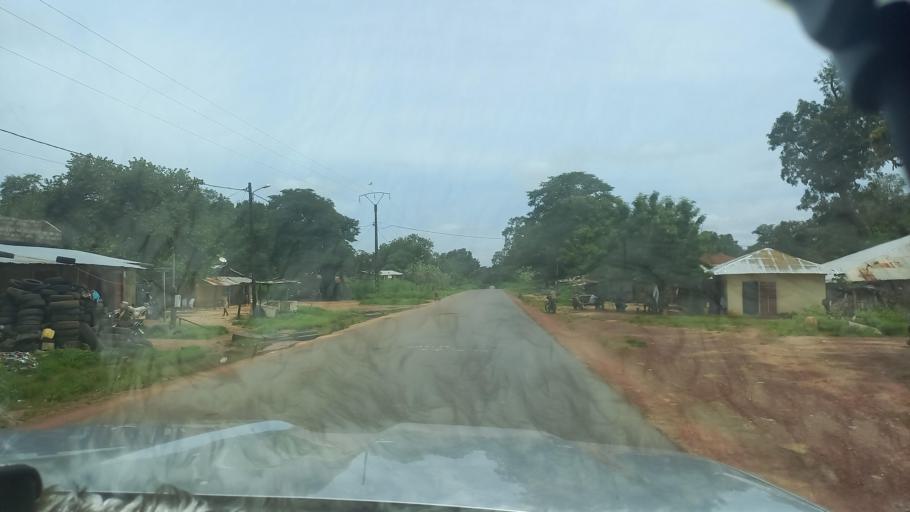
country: SN
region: Kolda
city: Marsassoum
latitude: 12.9645
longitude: -15.9724
